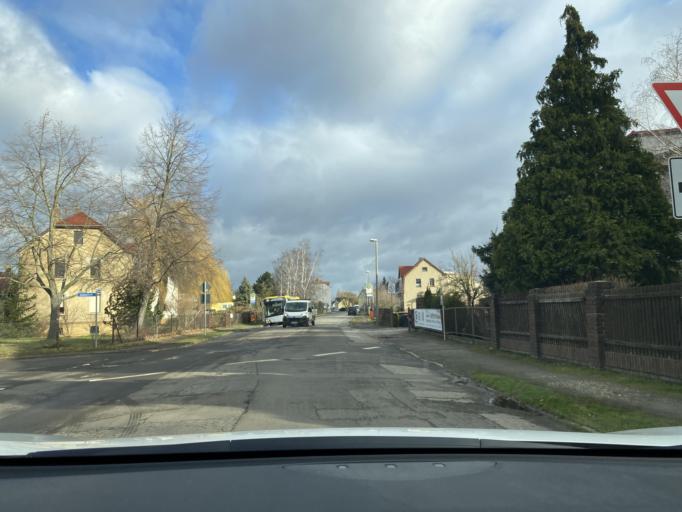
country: DE
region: Saxony
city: Zwenkau
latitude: 51.2615
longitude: 12.3063
